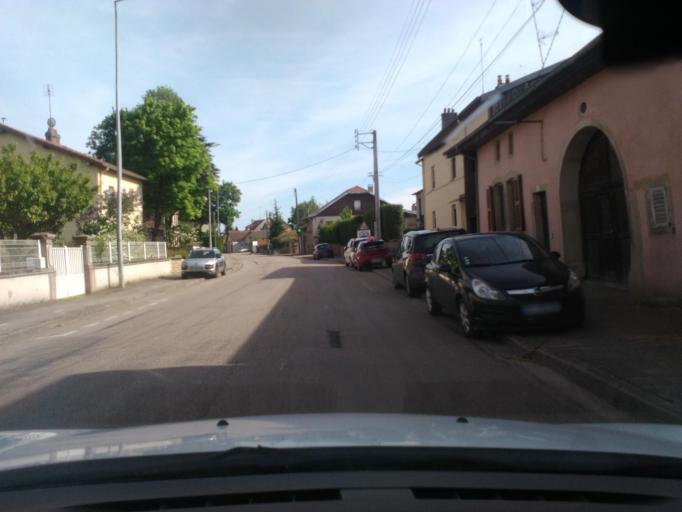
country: FR
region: Lorraine
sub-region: Departement des Vosges
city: Rambervillers
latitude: 48.3533
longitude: 6.6310
